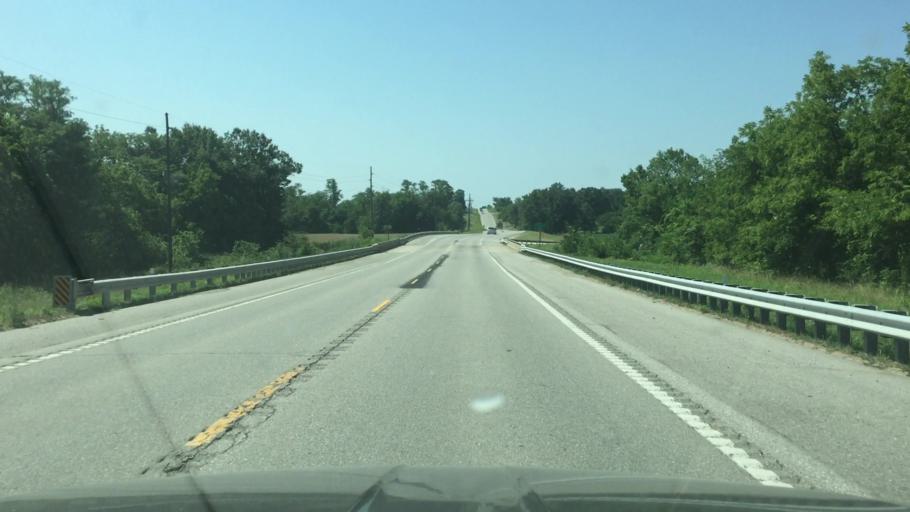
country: US
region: Missouri
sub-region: Moniteau County
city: Tipton
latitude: 38.6316
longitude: -92.7892
